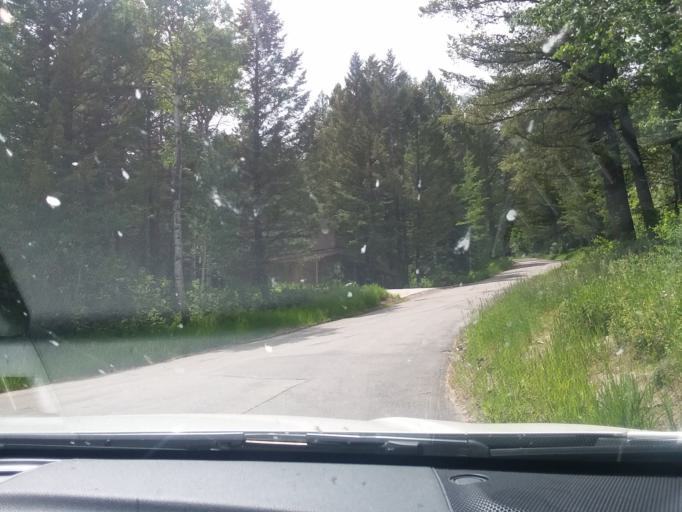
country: US
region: Wyoming
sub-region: Teton County
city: Moose Wilson Road
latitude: 43.5882
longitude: -110.8346
